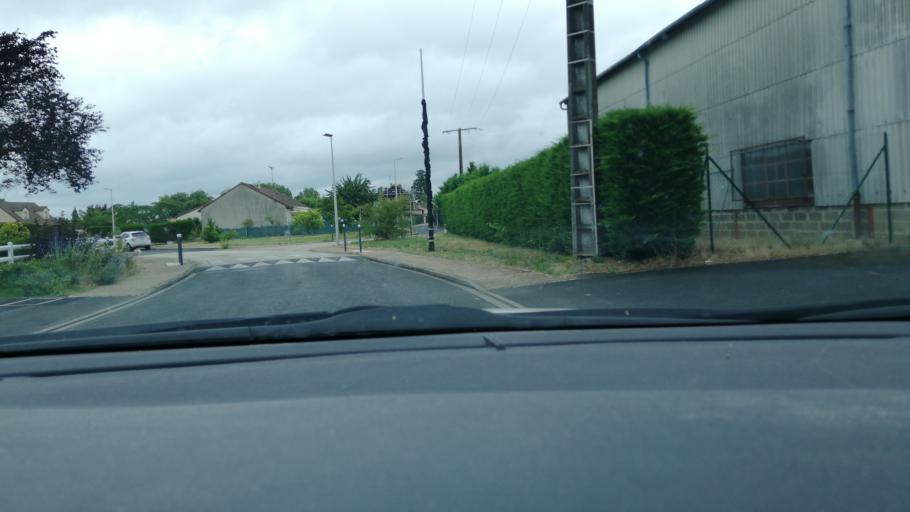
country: FR
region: Poitou-Charentes
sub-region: Departement de la Vienne
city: Antran
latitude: 46.8728
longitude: 0.5666
